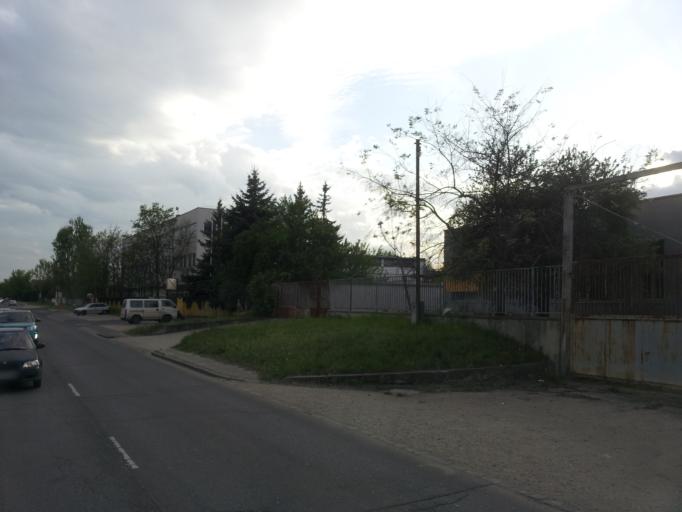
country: HU
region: Budapest
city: Budapest XV. keruelet
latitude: 47.5847
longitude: 19.1313
